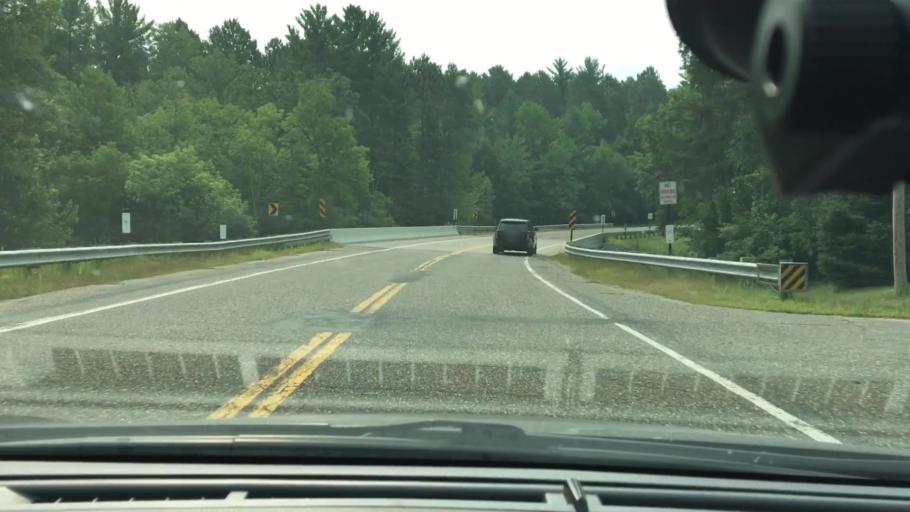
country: US
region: Minnesota
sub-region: Crow Wing County
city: Cross Lake
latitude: 46.6540
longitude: -94.0983
